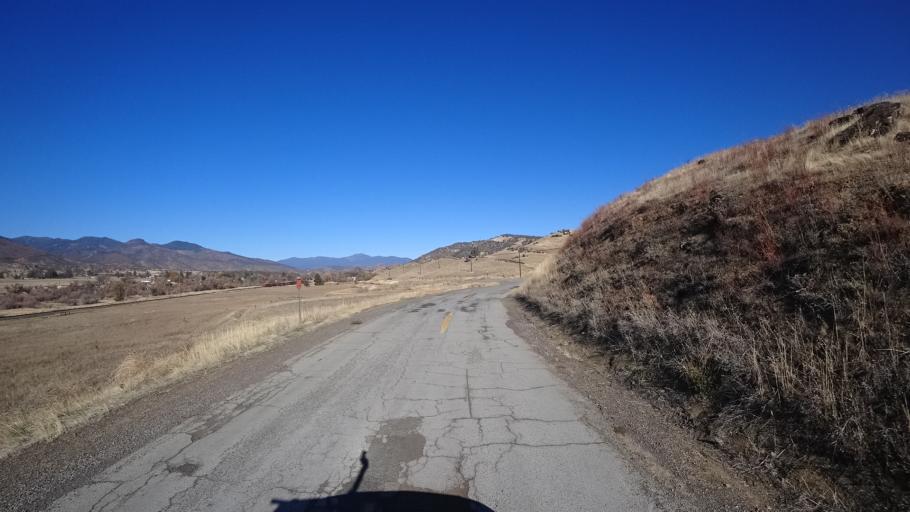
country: US
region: California
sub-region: Siskiyou County
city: Montague
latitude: 41.9032
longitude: -122.5469
